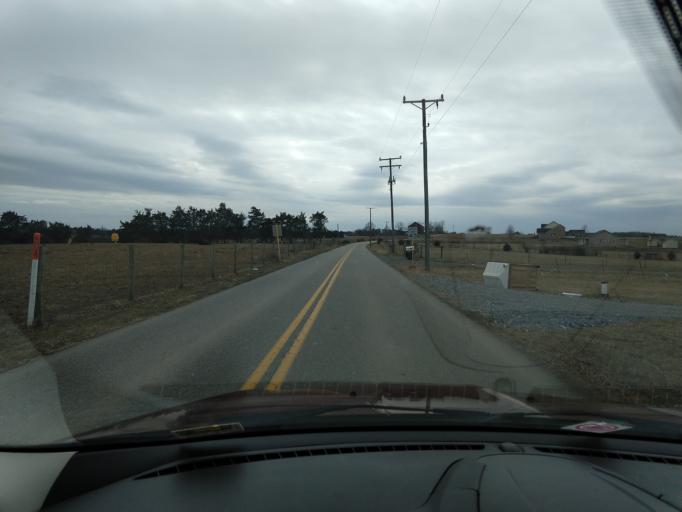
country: US
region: Virginia
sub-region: Augusta County
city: Crimora
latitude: 38.1883
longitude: -78.9125
